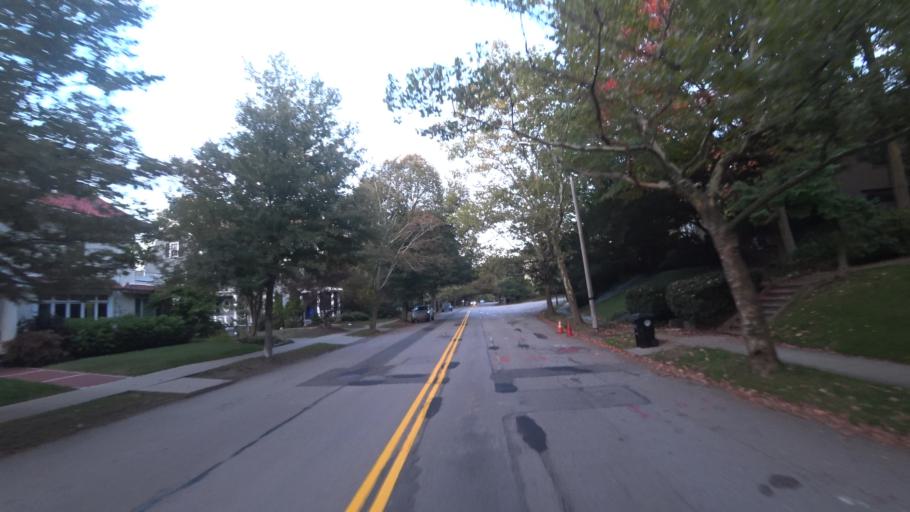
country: US
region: Massachusetts
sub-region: Norfolk County
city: Brookline
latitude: 42.3351
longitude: -71.1453
